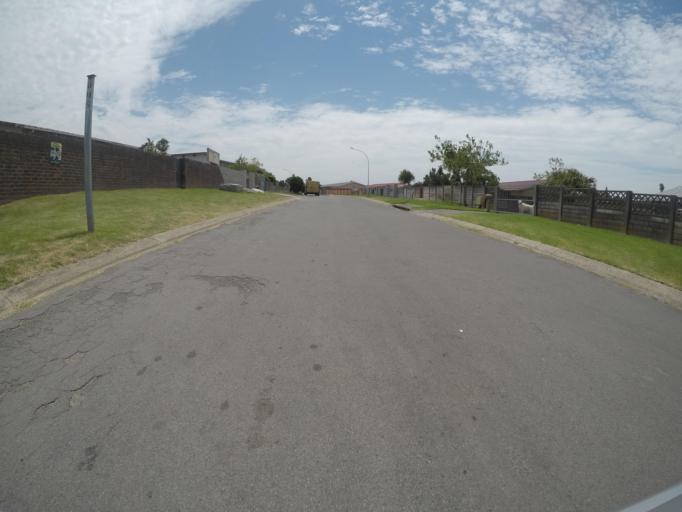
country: ZA
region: Eastern Cape
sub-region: Buffalo City Metropolitan Municipality
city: East London
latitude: -32.9795
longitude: 27.8648
